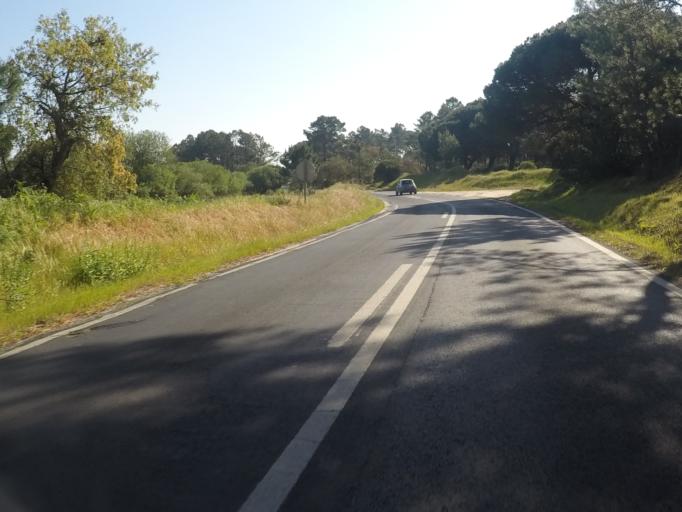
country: PT
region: Setubal
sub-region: Sesimbra
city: Sesimbra
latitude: 38.5276
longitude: -9.1315
